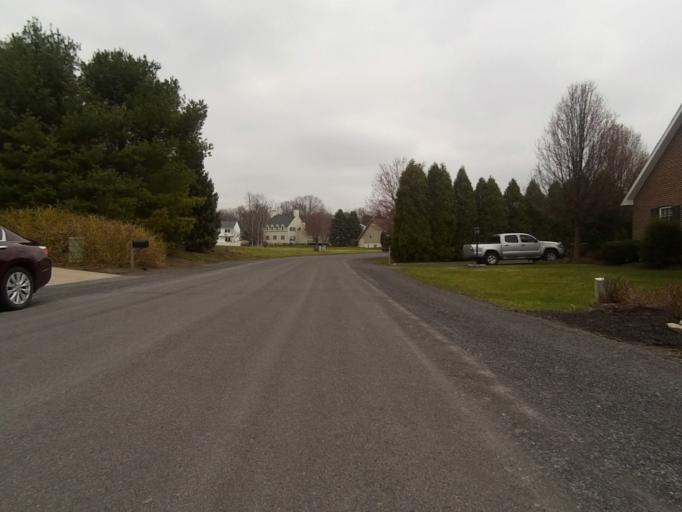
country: US
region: Pennsylvania
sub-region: Centre County
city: Boalsburg
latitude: 40.7853
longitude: -77.7803
